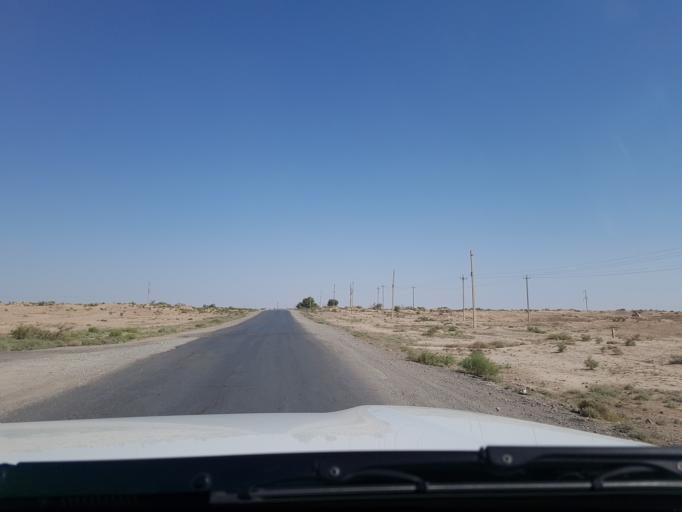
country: IR
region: Razavi Khorasan
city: Sarakhs
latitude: 36.5228
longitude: 61.2412
